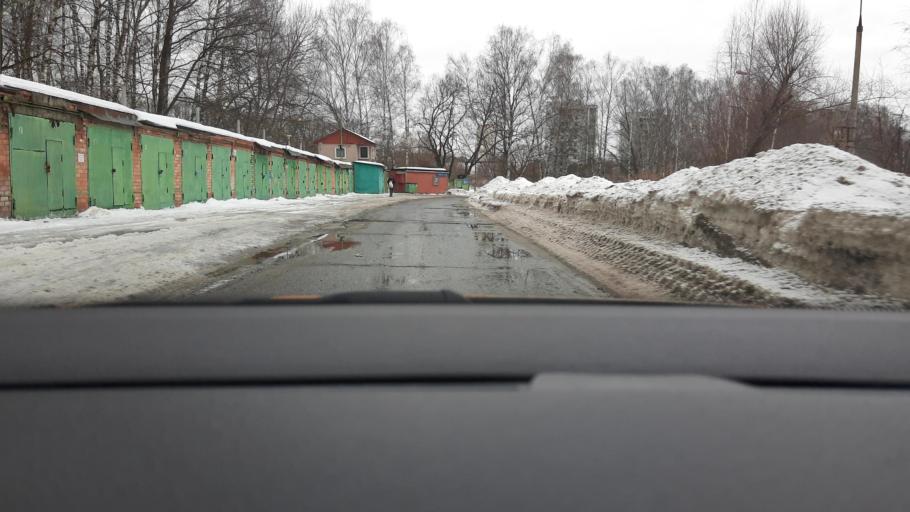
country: RU
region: Moscow
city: Babushkin
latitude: 55.8497
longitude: 37.7023
